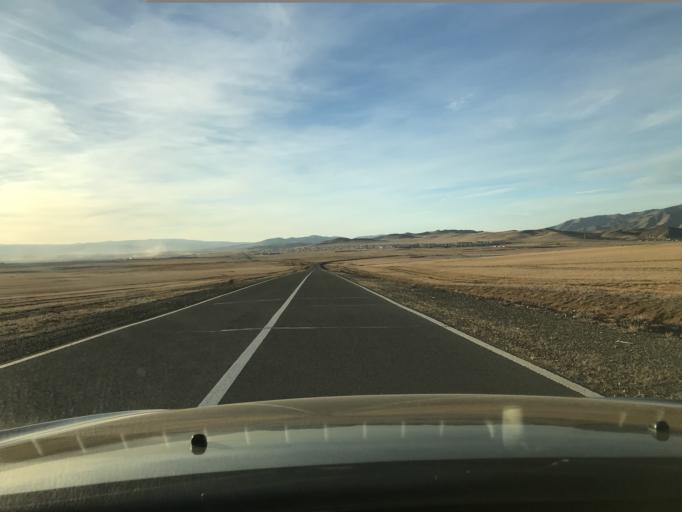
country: MN
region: Central Aimak
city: Arhust
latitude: 47.7645
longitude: 107.4306
